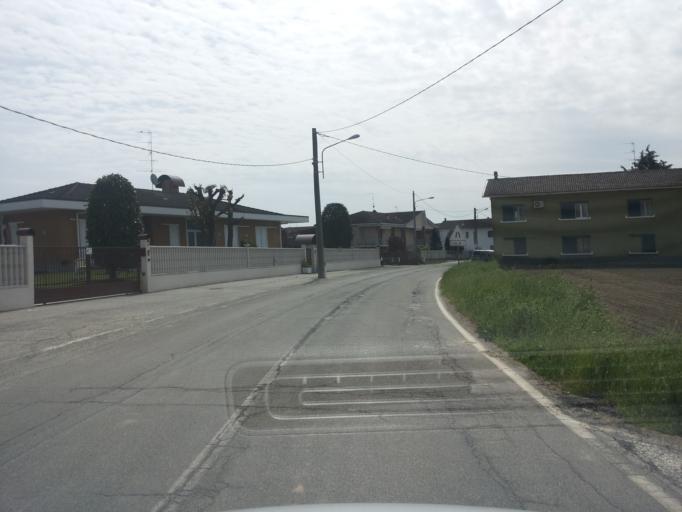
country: IT
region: Piedmont
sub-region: Provincia di Vercelli
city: Motta De Conti
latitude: 45.1962
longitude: 8.5176
